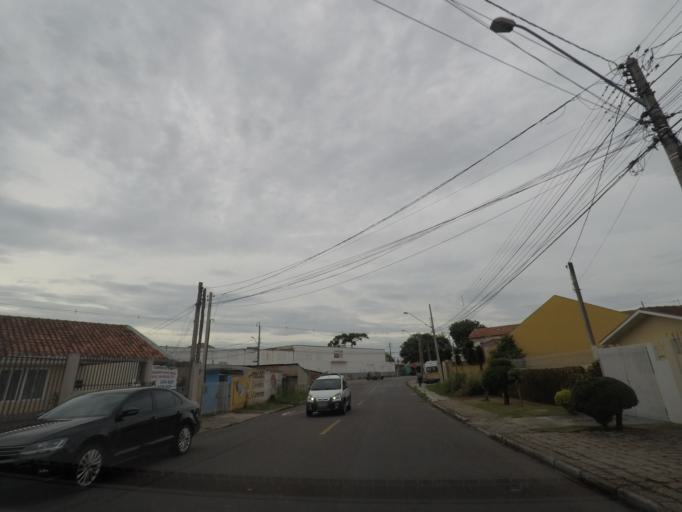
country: BR
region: Parana
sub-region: Curitiba
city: Curitiba
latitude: -25.4728
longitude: -49.3026
